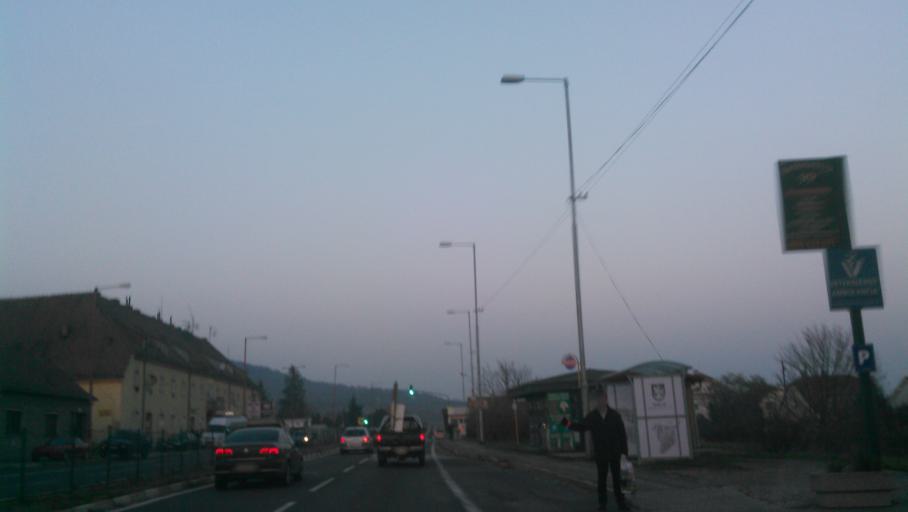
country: SK
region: Bratislavsky
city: Svaty Jur
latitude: 48.2515
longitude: 17.2150
